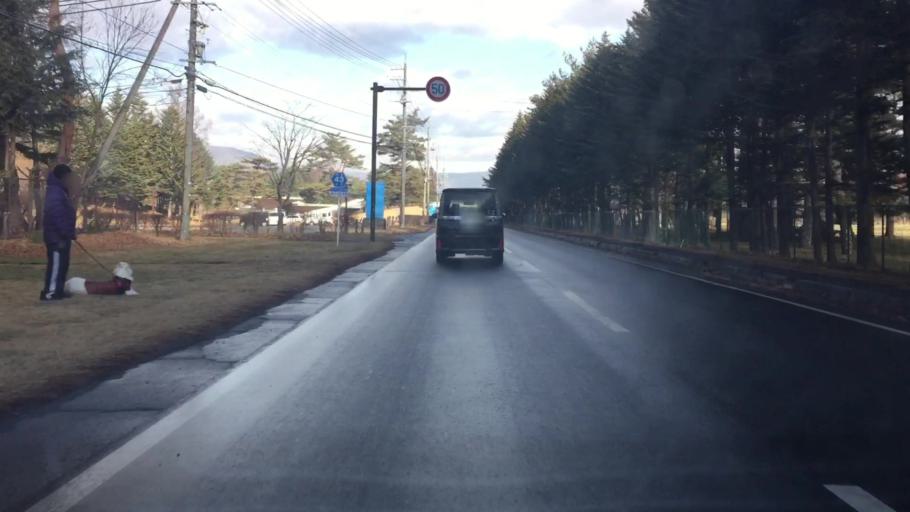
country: JP
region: Nagano
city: Saku
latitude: 36.3084
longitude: 138.6316
